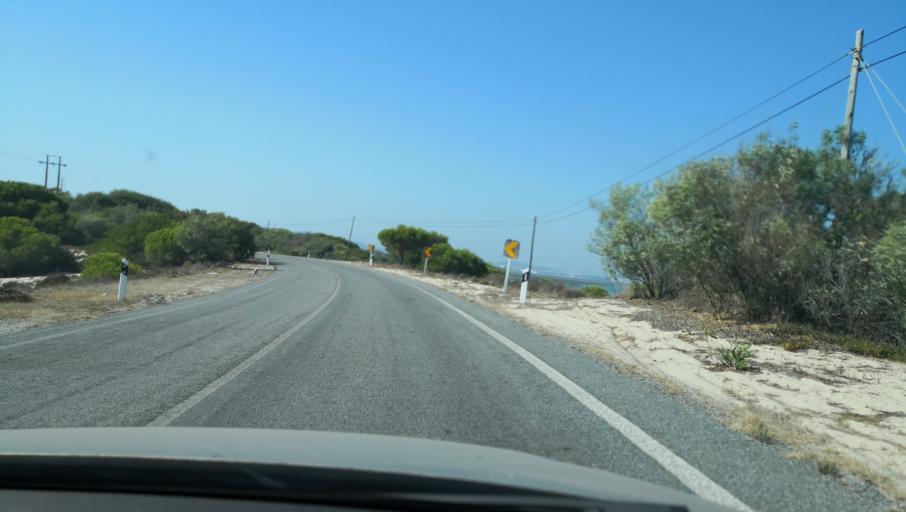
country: PT
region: Setubal
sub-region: Setubal
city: Setubal
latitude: 38.4173
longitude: -8.8165
